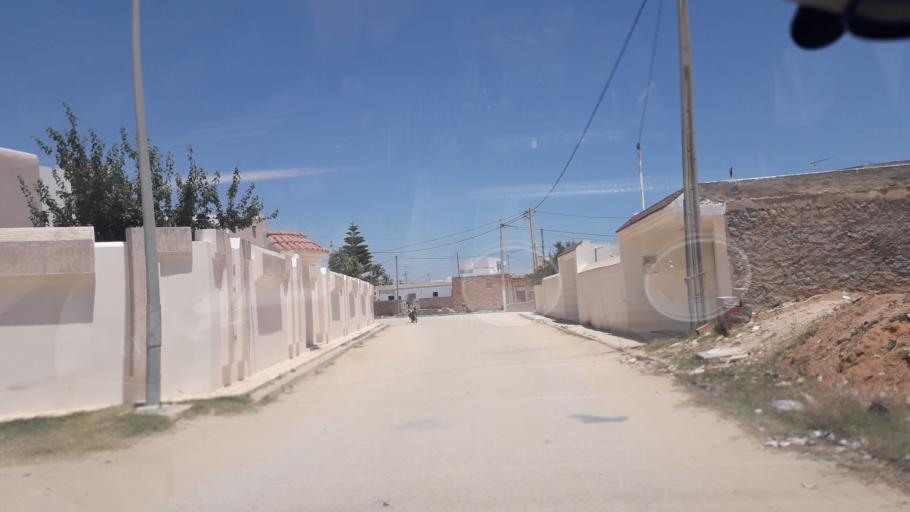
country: TN
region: Safaqis
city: Al Qarmadah
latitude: 34.8177
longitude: 10.7691
